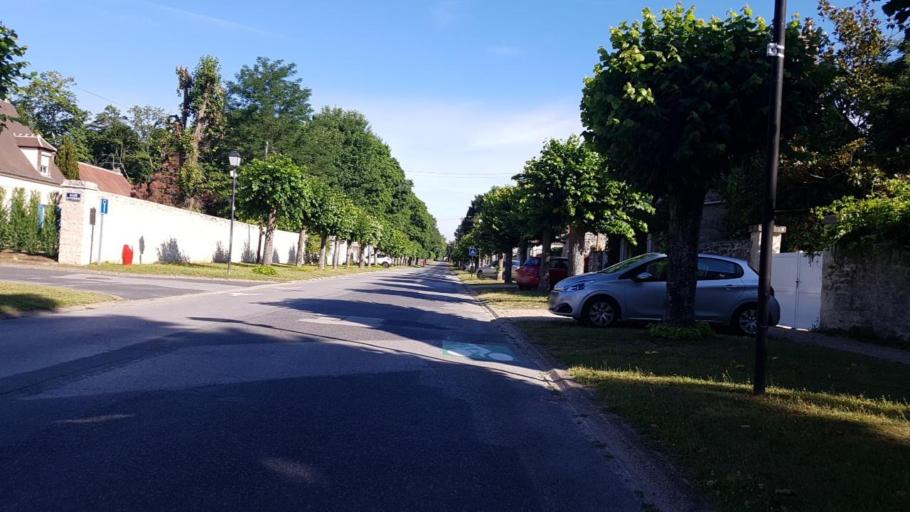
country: FR
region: Picardie
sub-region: Departement de l'Oise
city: Chamant
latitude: 49.2233
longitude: 2.6081
